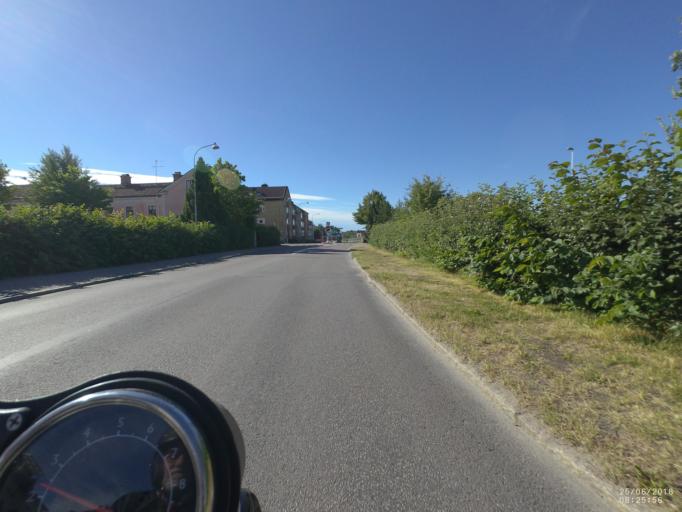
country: SE
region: Soedermanland
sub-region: Nykopings Kommun
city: Nykoping
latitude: 58.7537
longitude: 16.9975
